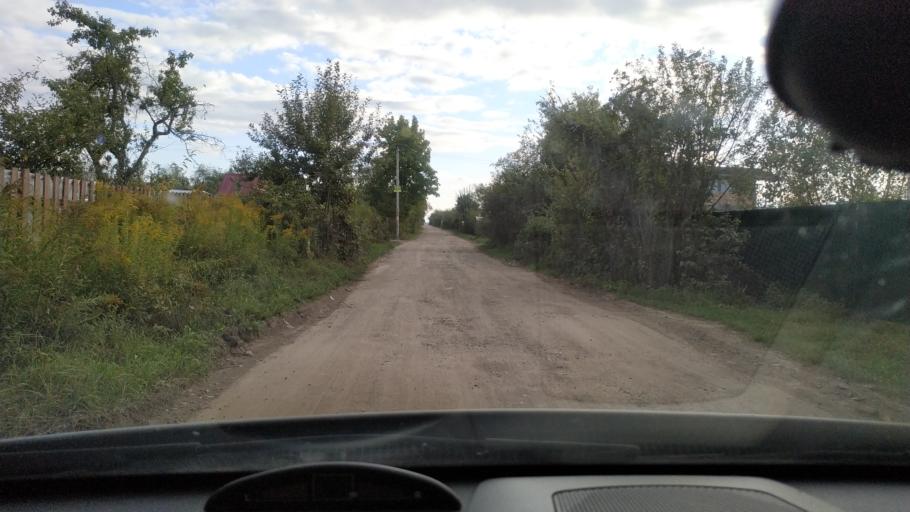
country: RU
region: Rjazan
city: Polyany
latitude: 54.5580
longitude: 39.8767
